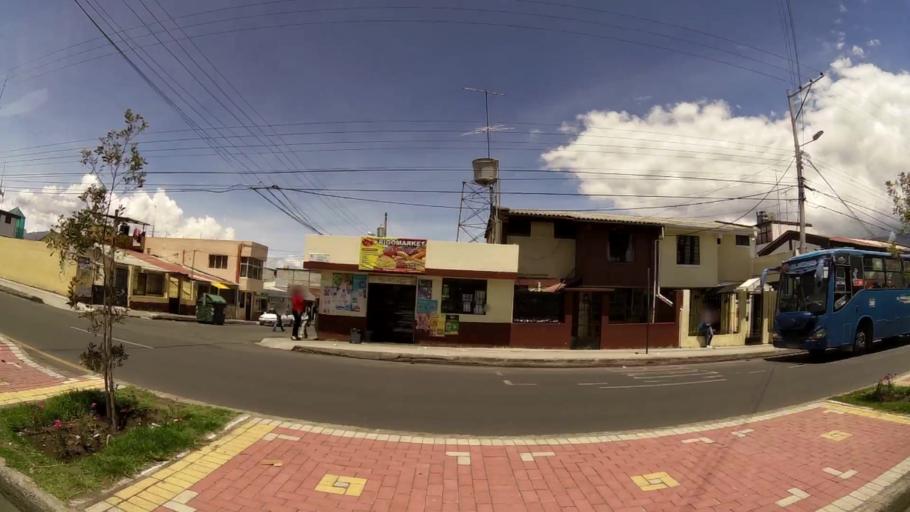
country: EC
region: Chimborazo
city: Riobamba
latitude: -1.6814
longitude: -78.6390
